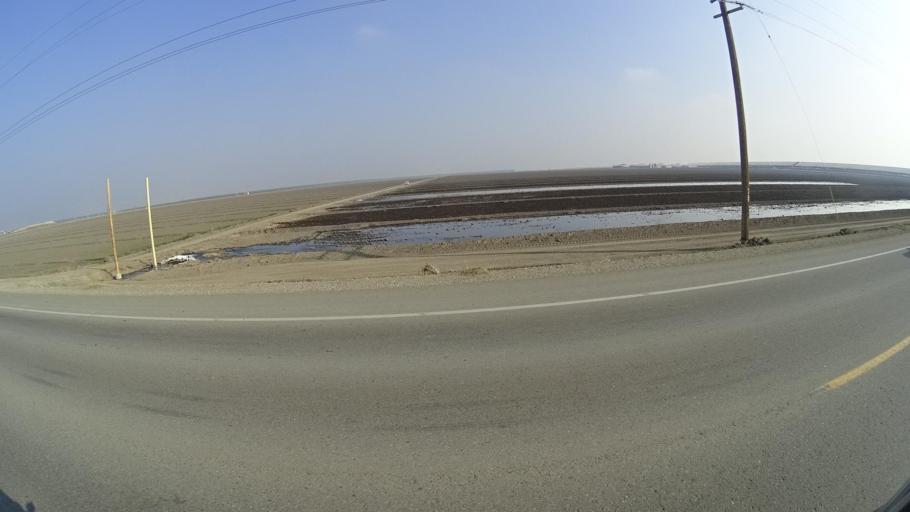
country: US
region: California
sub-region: Kern County
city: Greenfield
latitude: 35.1759
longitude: -119.1100
